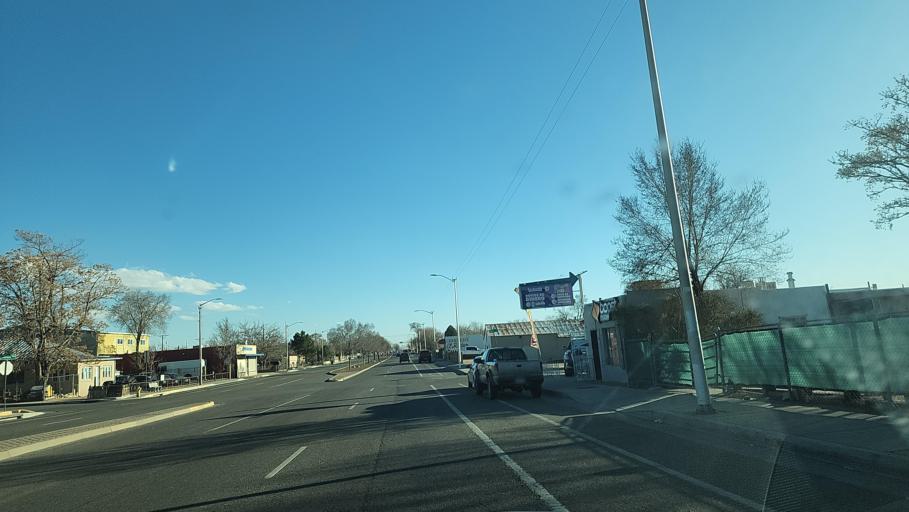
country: US
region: New Mexico
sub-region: Bernalillo County
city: Albuquerque
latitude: 35.0661
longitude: -106.6456
